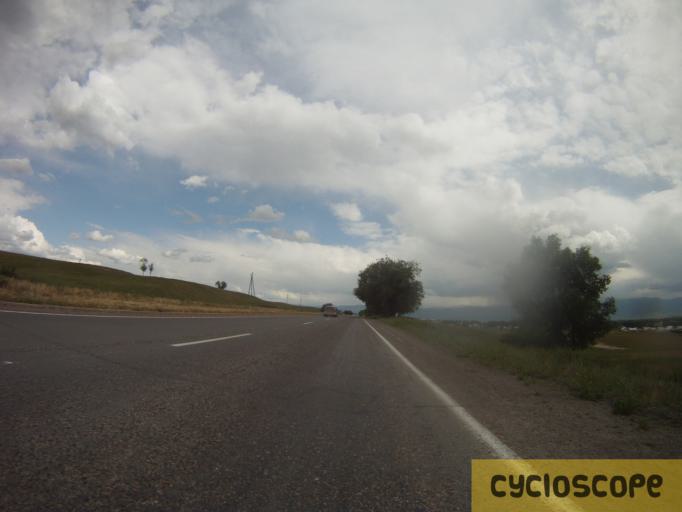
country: KZ
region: Almaty Oblysy
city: Burunday
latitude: 43.2597
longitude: 76.3122
